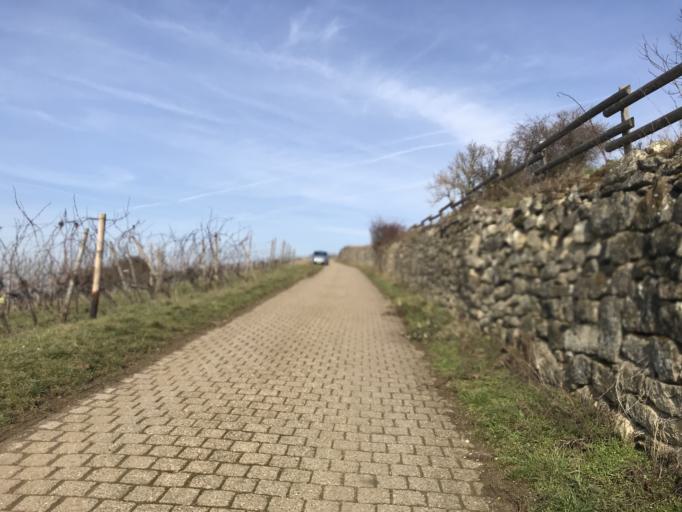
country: DE
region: Rheinland-Pfalz
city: Schwabenheim
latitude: 49.9473
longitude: 8.0815
